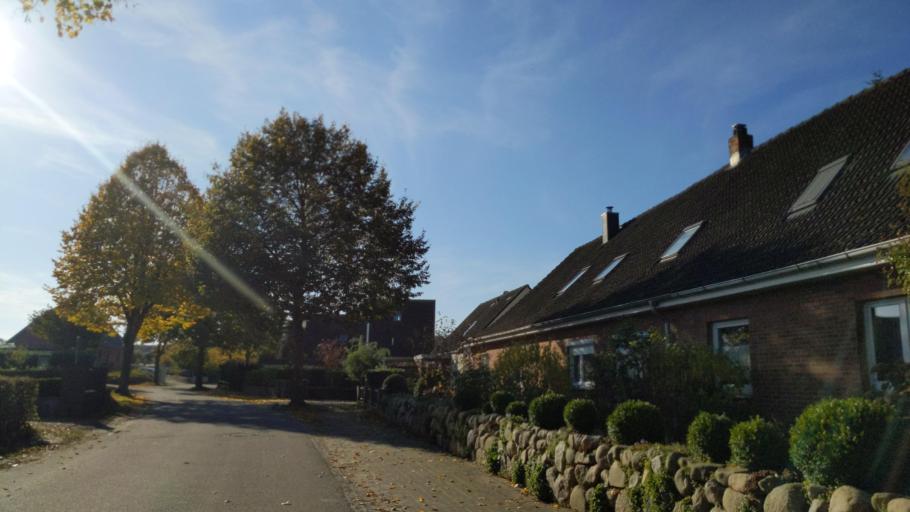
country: DE
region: Schleswig-Holstein
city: Kasseedorf
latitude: 54.1359
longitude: 10.7047
